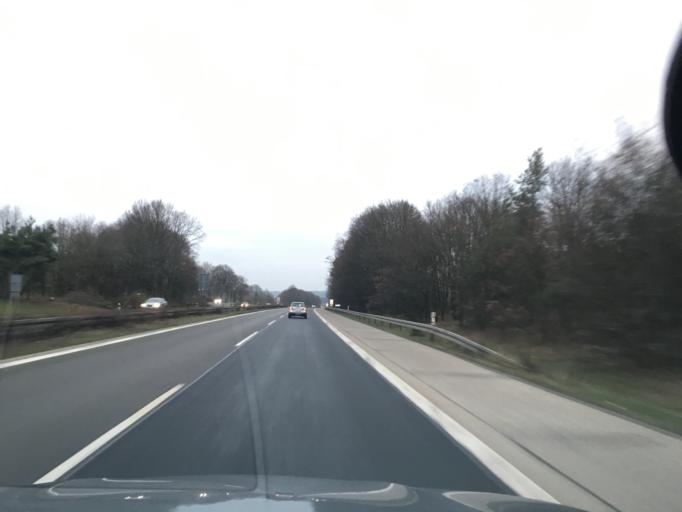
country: DE
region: Bavaria
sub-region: Regierungsbezirk Mittelfranken
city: Gremsdorf
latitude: 49.6773
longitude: 10.8693
